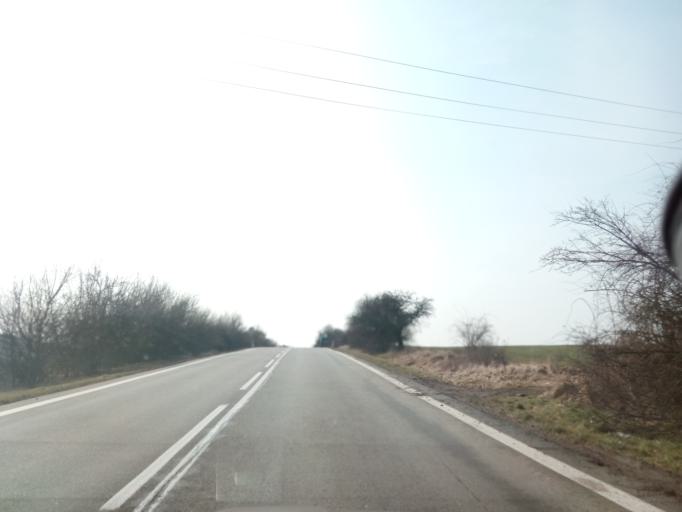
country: HU
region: Borsod-Abauj-Zemplen
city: Satoraljaujhely
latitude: 48.5137
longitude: 21.6579
